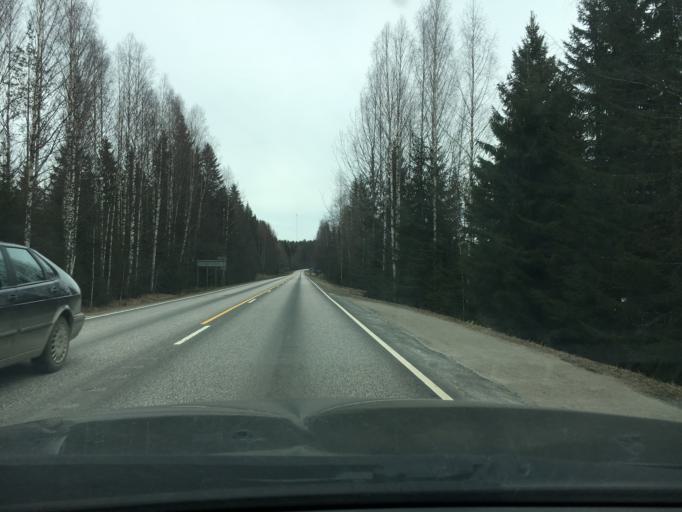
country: FI
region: Central Finland
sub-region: AEaenekoski
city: Sumiainen
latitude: 62.5766
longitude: 26.0884
